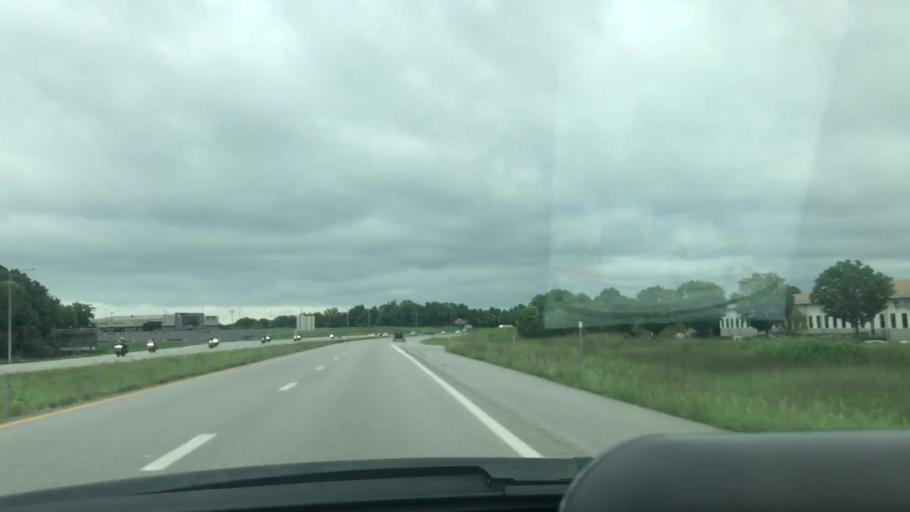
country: US
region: Missouri
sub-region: Greene County
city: Springfield
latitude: 37.2467
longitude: -93.3473
